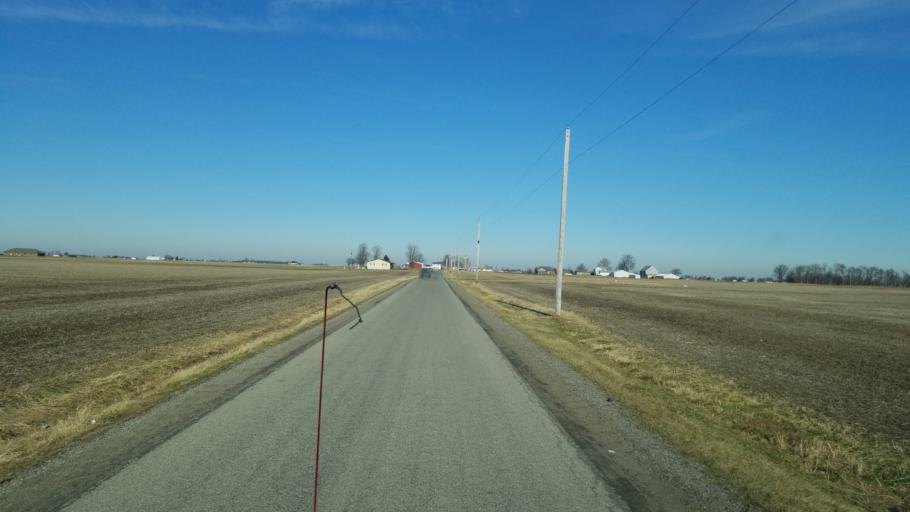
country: US
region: Ohio
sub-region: Putnam County
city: Leipsic
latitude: 41.0801
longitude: -84.0102
